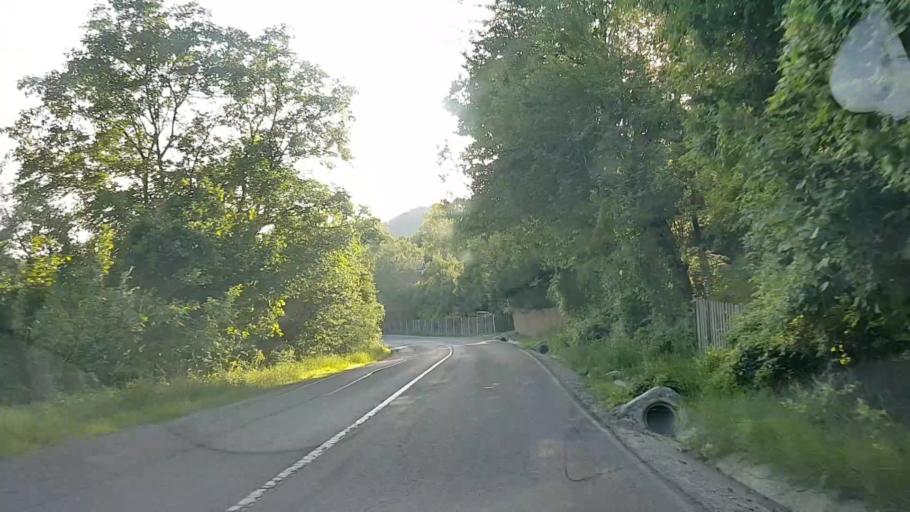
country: RO
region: Harghita
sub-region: Comuna Praid
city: Ocna de Sus
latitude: 46.5731
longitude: 25.2102
